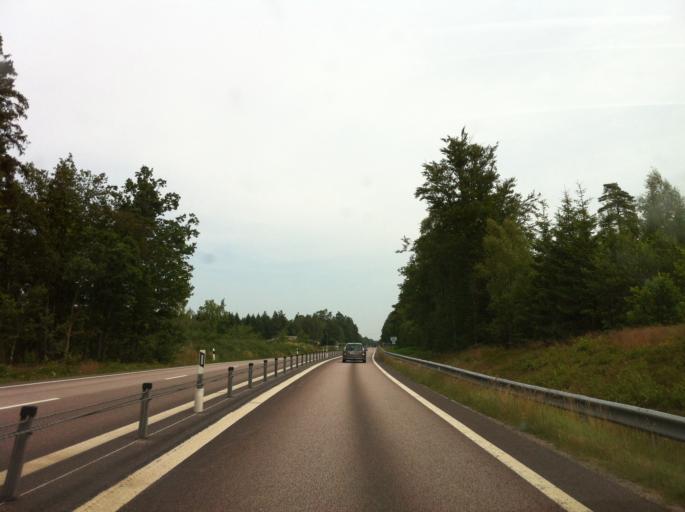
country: SE
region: Kalmar
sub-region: Torsas Kommun
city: Torsas
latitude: 56.2843
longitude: 15.9817
